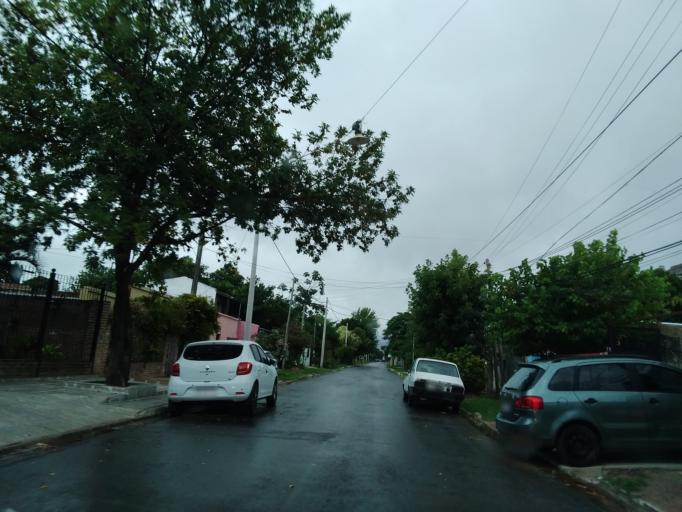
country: AR
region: Corrientes
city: Corrientes
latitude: -27.4946
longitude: -58.8230
